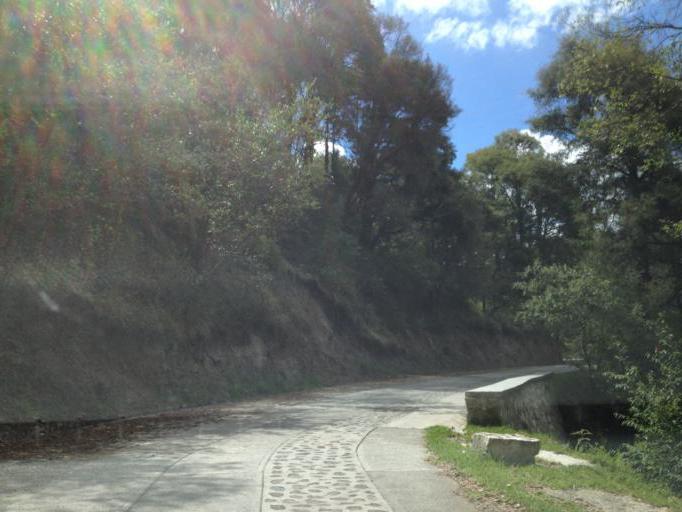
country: MX
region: Hidalgo
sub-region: Pachuca de Soto
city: San Miguel Cerezo (El Cerezo)
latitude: 20.2116
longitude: -98.6856
